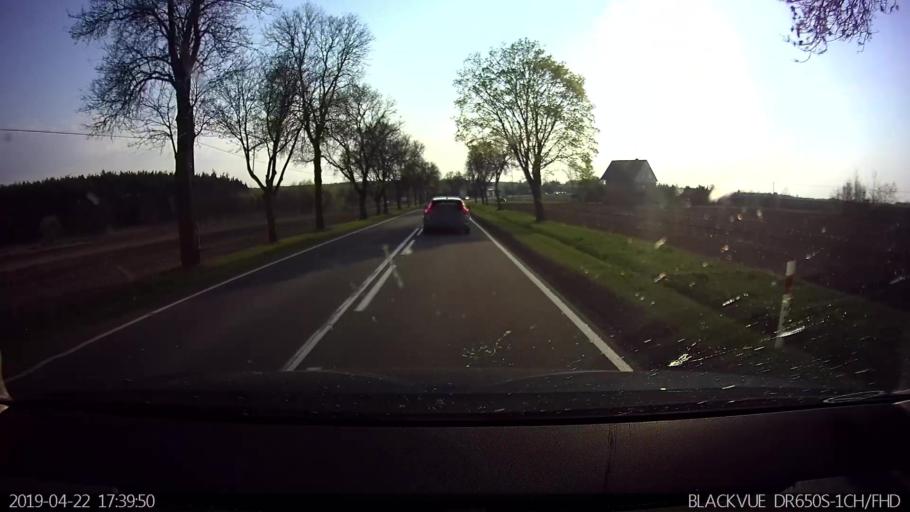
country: PL
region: Masovian Voivodeship
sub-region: Powiat wegrowski
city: Miedzna
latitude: 52.3996
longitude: 22.1347
